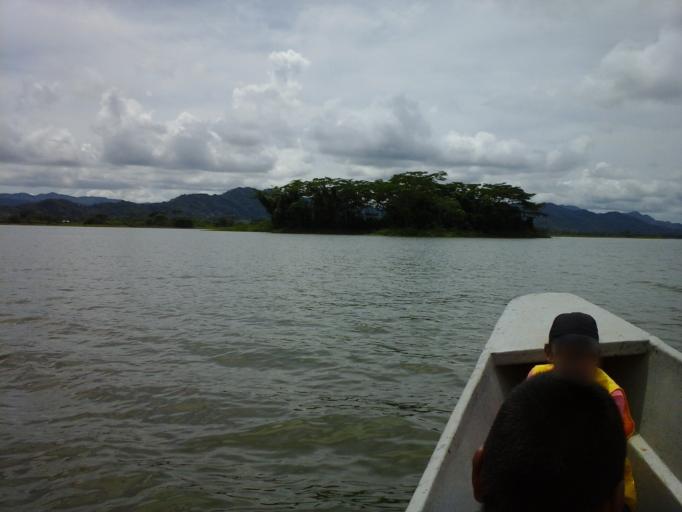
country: CO
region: Bolivar
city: San Cristobal
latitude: 9.8750
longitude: -75.3011
